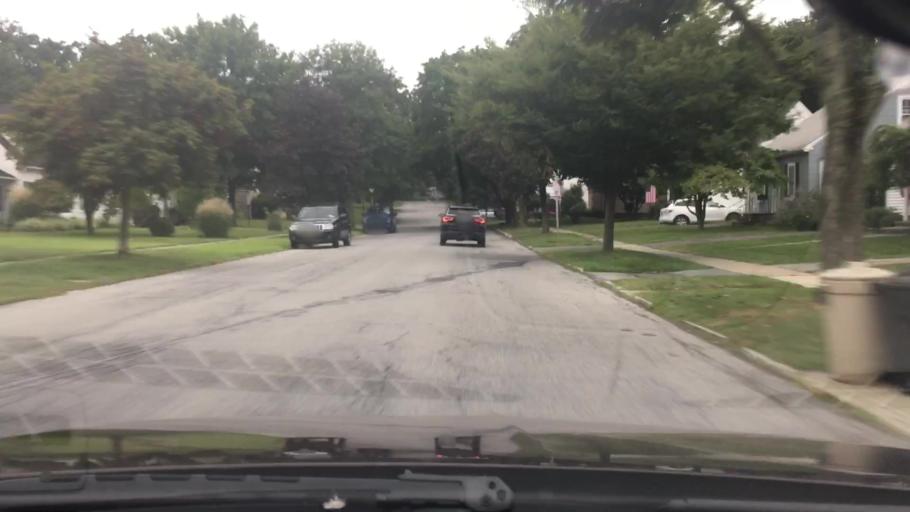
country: US
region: New York
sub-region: Dutchess County
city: Arlington
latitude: 41.6823
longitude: -73.9114
